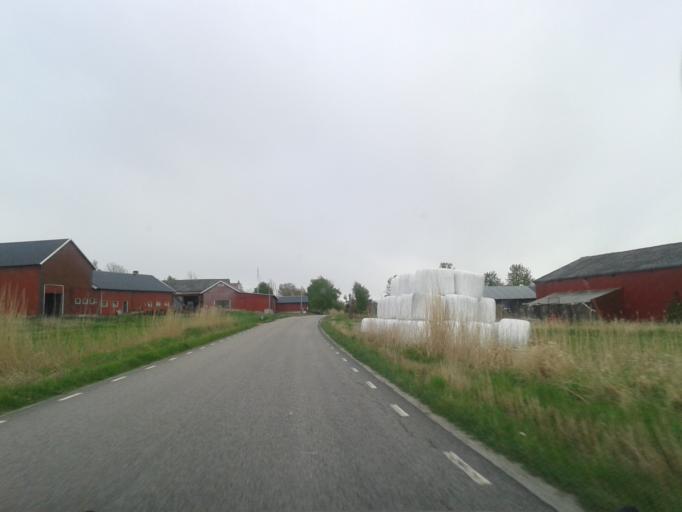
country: SE
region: Vaestra Goetaland
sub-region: Kungalvs Kommun
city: Kode
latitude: 57.9480
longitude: 11.8193
